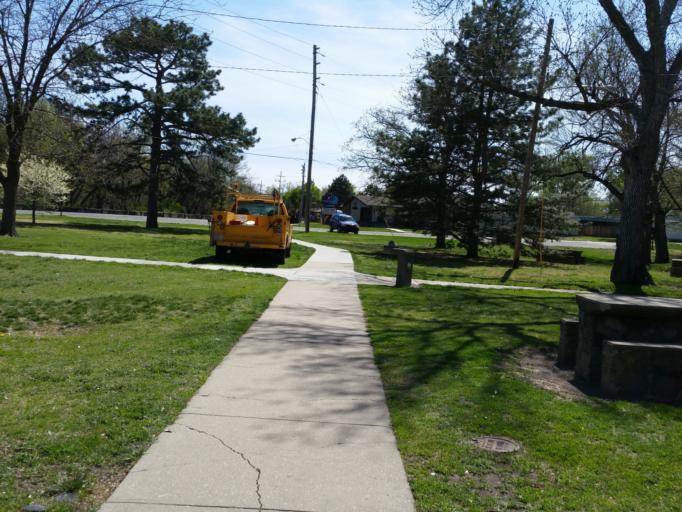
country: US
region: Kansas
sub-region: Saline County
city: Salina
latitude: 38.8323
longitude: -97.6039
